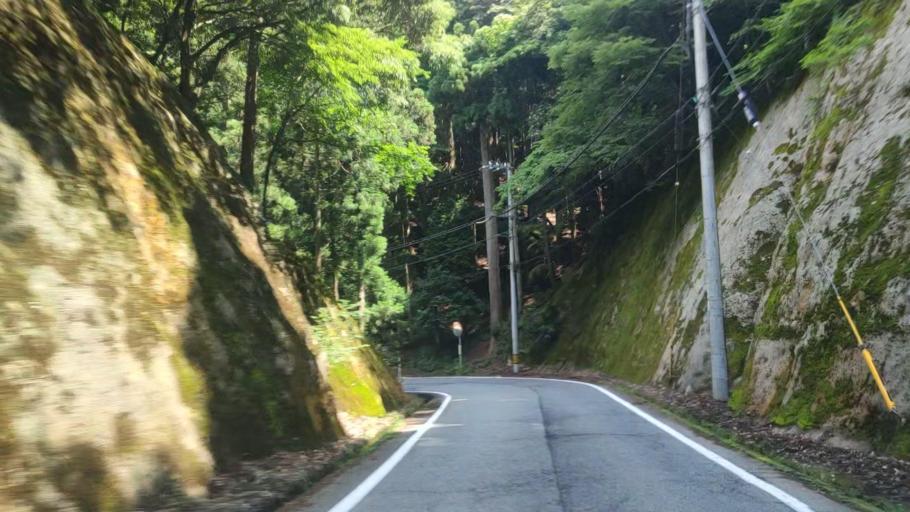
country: JP
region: Hyogo
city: Toyooka
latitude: 35.6414
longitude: 134.7660
